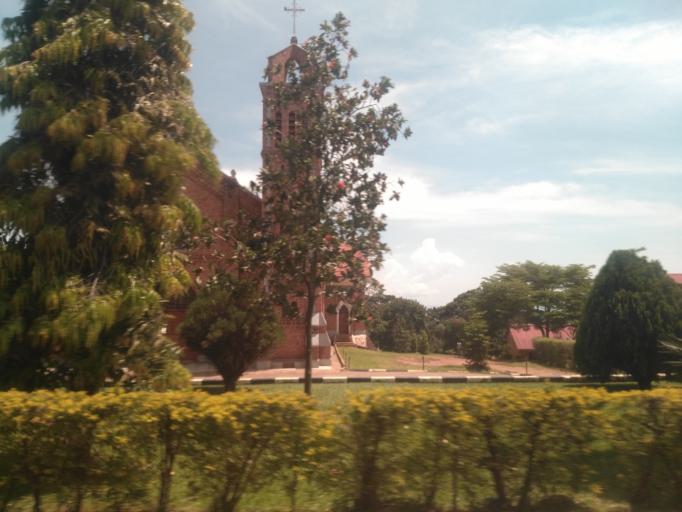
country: UG
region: Central Region
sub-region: Wakiso District
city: Entebbe
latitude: 0.0442
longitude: 32.4654
